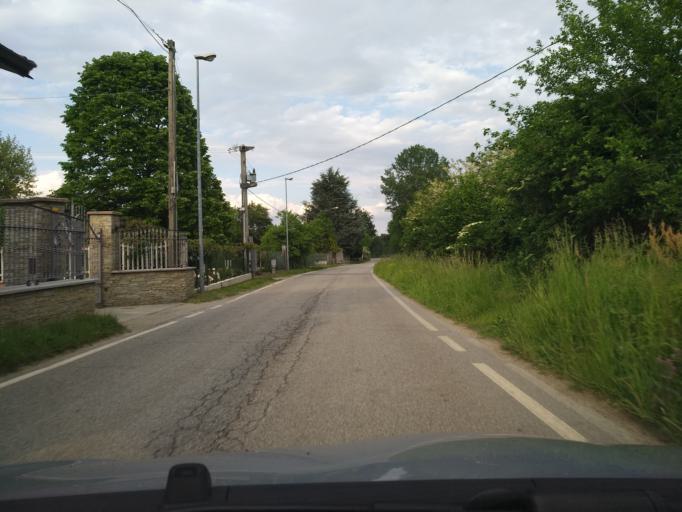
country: IT
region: Piedmont
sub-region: Provincia di Torino
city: Roletto
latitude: 44.9096
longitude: 7.3470
